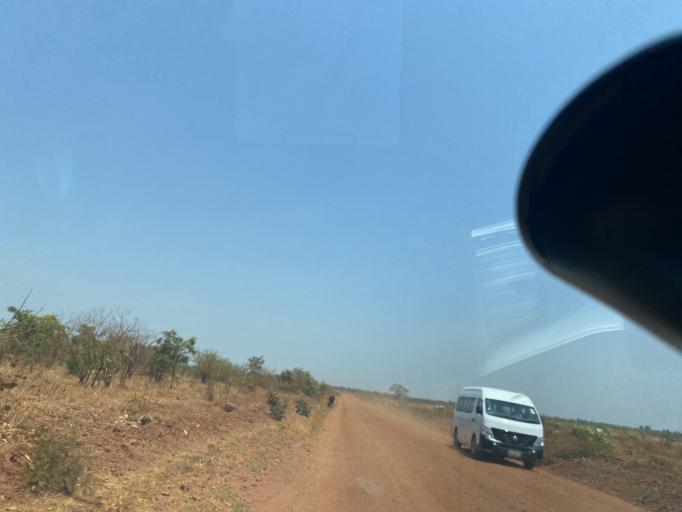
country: ZM
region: Southern
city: Nakambala
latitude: -15.5033
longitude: 27.9230
